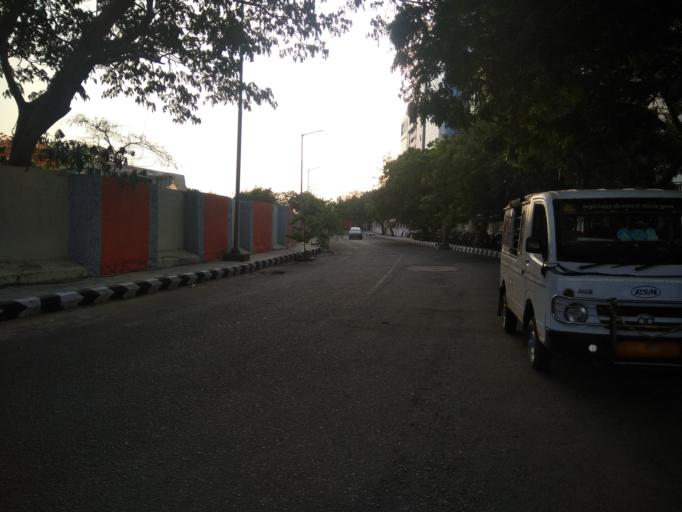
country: IN
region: Tamil Nadu
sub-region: Chennai
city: Gandhi Nagar
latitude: 12.9890
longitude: 80.2507
